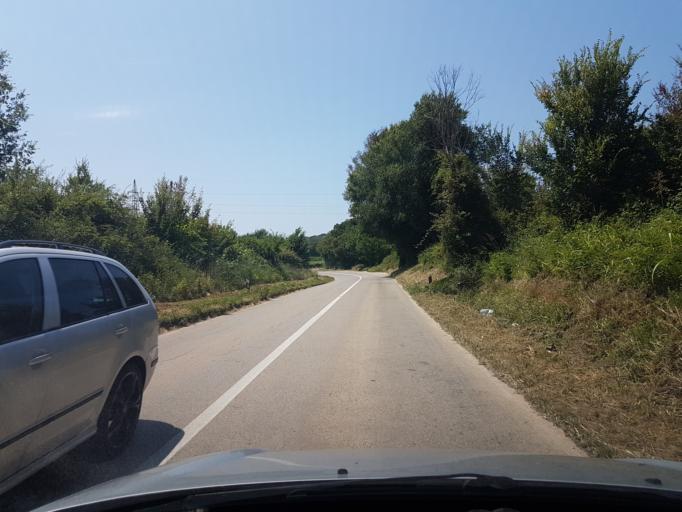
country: HR
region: Istarska
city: Vrsar
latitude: 45.1504
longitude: 13.6283
